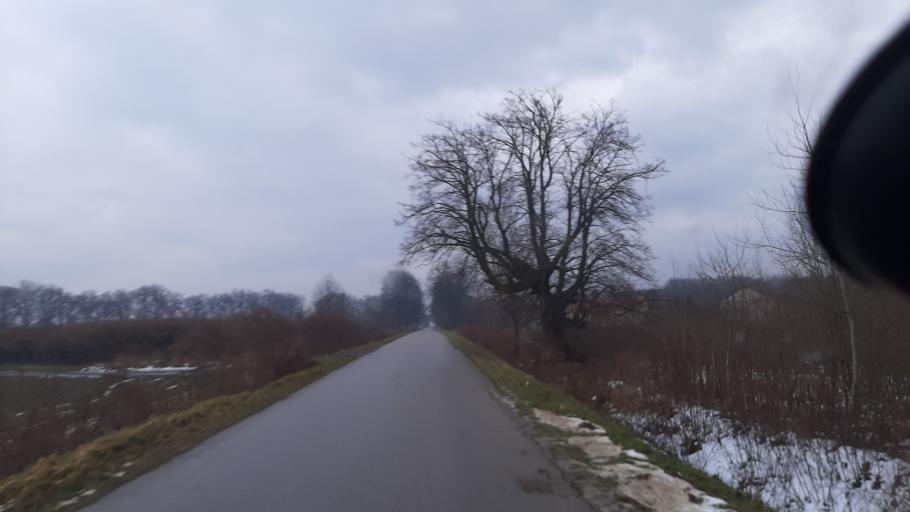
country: PL
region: Lublin Voivodeship
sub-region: Powiat lubelski
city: Lublin
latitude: 51.3356
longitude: 22.5478
